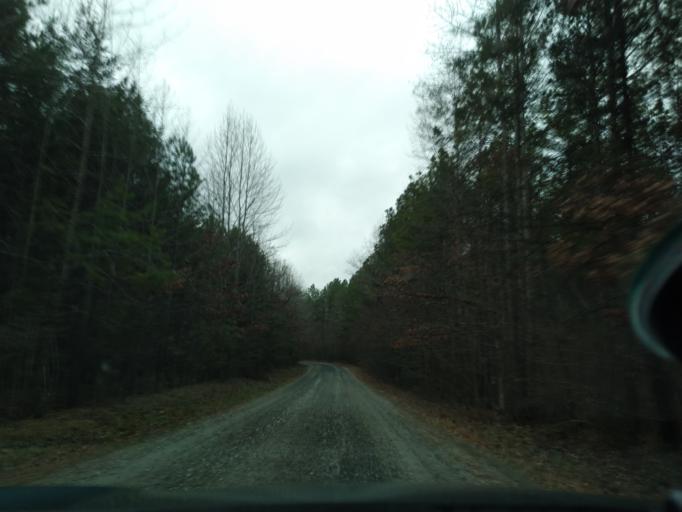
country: US
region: Virginia
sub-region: Buckingham County
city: Buckingham
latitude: 37.4319
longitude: -78.6558
